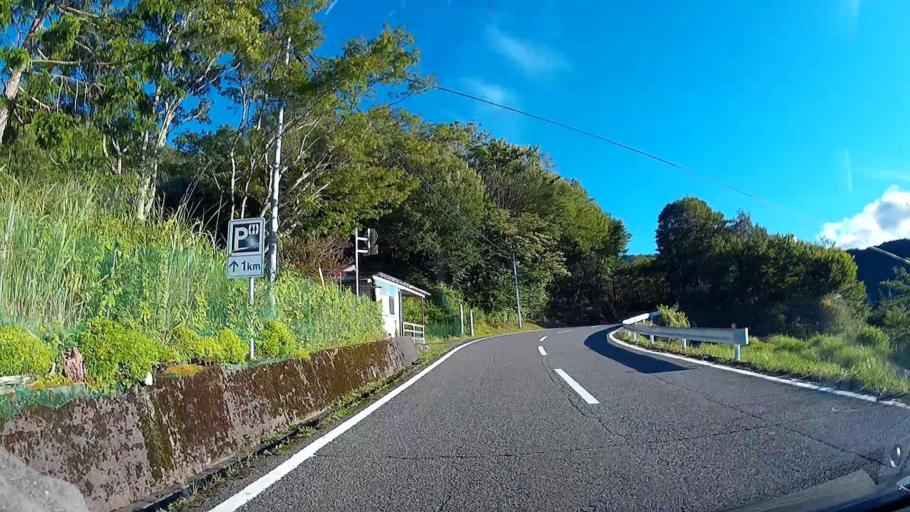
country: JP
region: Shizuoka
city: Shizuoka-shi
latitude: 35.1902
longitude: 138.2500
